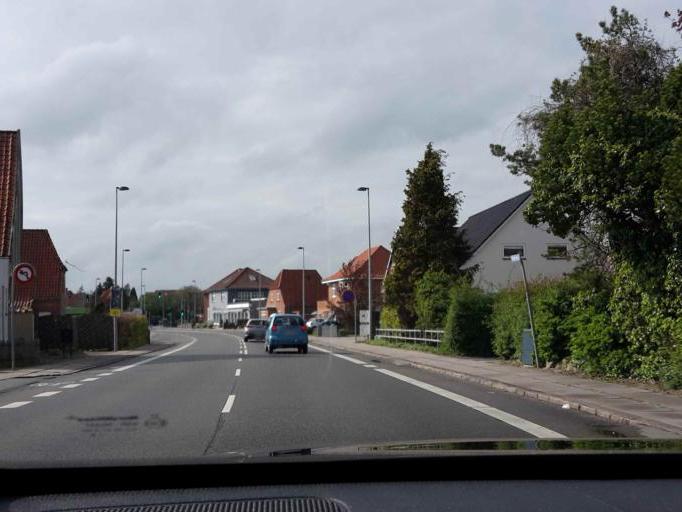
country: DK
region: South Denmark
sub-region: Odense Kommune
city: Odense
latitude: 55.4062
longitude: 10.3518
